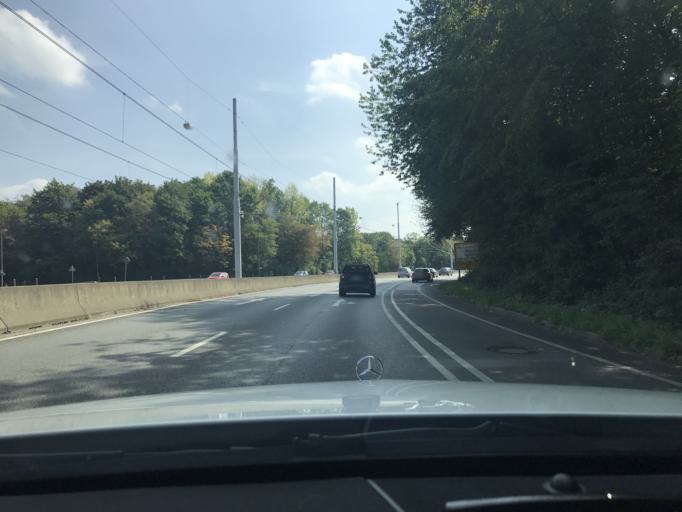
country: DE
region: North Rhine-Westphalia
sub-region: Regierungsbezirk Arnsberg
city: Bochum
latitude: 51.4544
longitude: 7.2445
